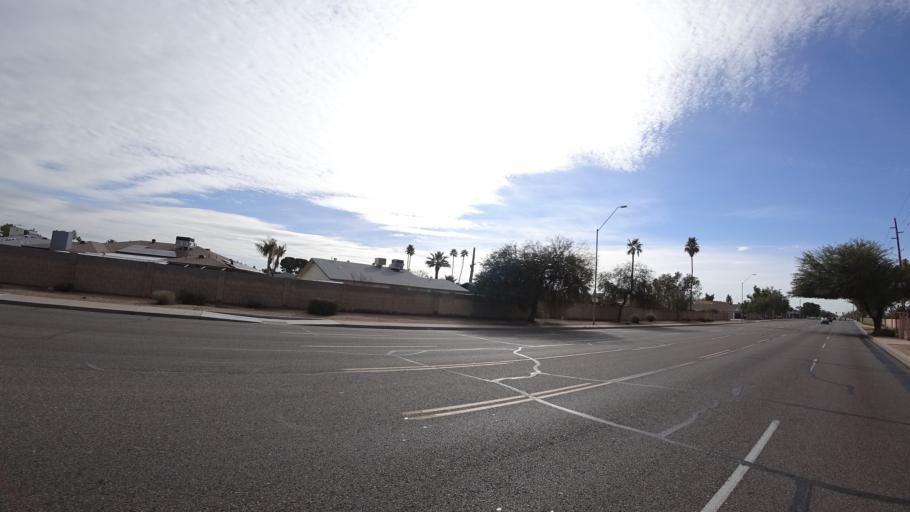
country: US
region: Arizona
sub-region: Maricopa County
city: Glendale
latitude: 33.6139
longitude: -112.1513
